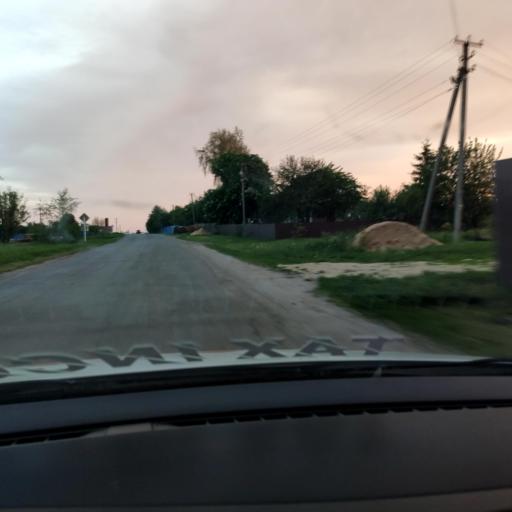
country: RU
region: Voronezj
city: Maslovka
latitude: 51.4518
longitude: 39.2434
